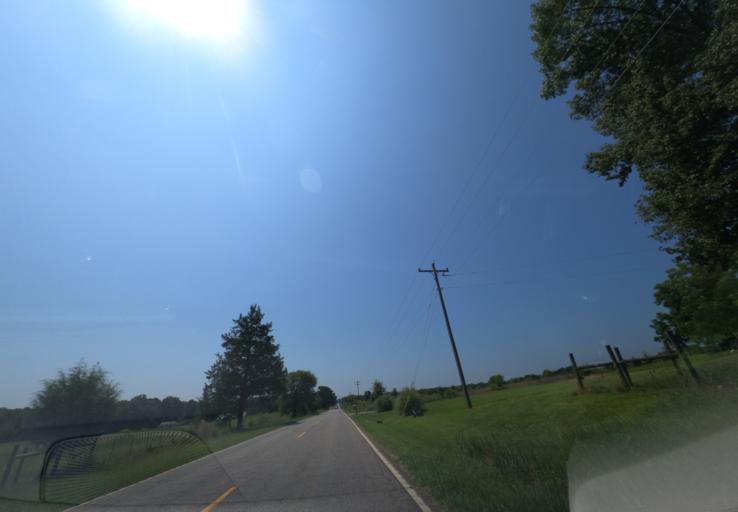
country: US
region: South Carolina
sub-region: Greenwood County
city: Greenwood
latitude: 34.0277
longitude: -82.1287
